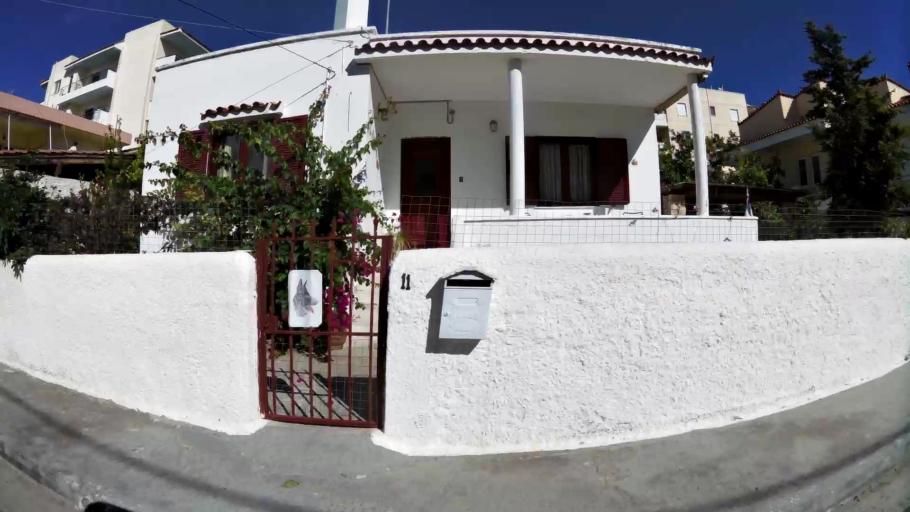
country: GR
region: Attica
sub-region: Nomarchia Anatolikis Attikis
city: Markopoulo
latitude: 37.8751
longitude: 23.9341
